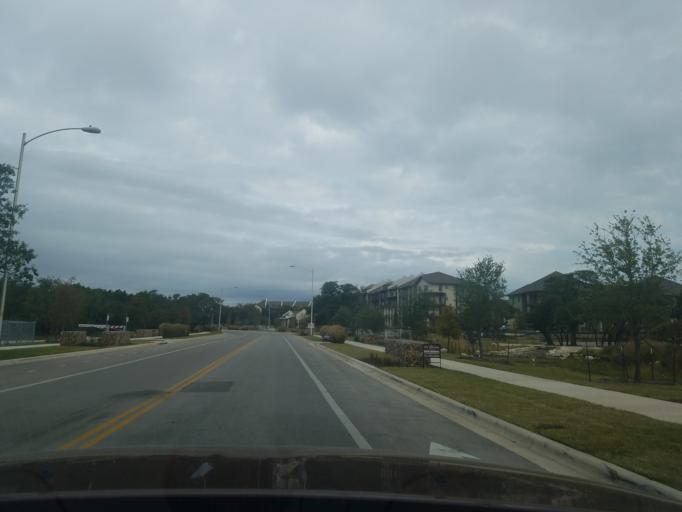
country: US
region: Texas
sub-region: Williamson County
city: Anderson Mill
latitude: 30.4733
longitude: -97.7841
